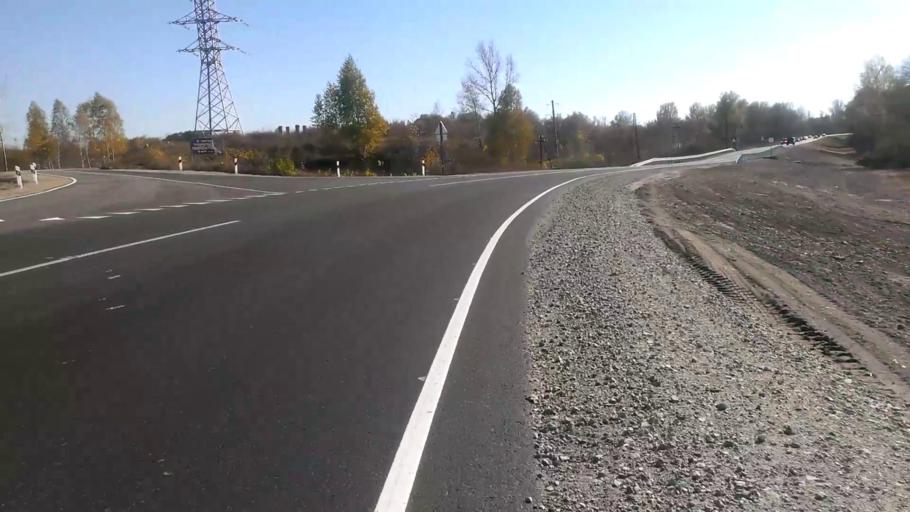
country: RU
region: Altai Krai
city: Sannikovo
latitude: 53.3280
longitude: 83.9410
